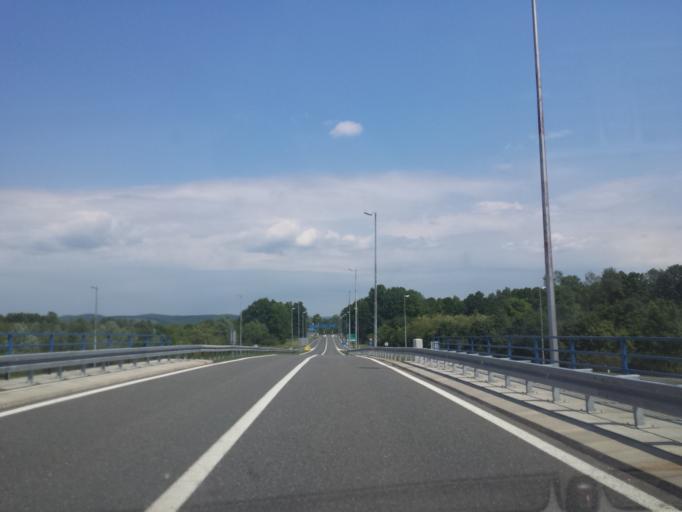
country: HR
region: Brodsko-Posavska
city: Batrina
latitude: 45.1670
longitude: 17.6770
